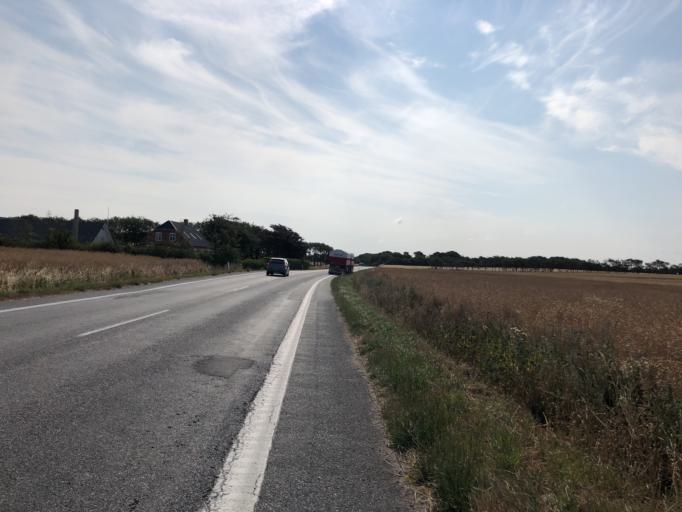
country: DK
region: Central Jutland
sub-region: Holstebro Kommune
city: Vinderup
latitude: 56.5885
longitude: 8.7974
